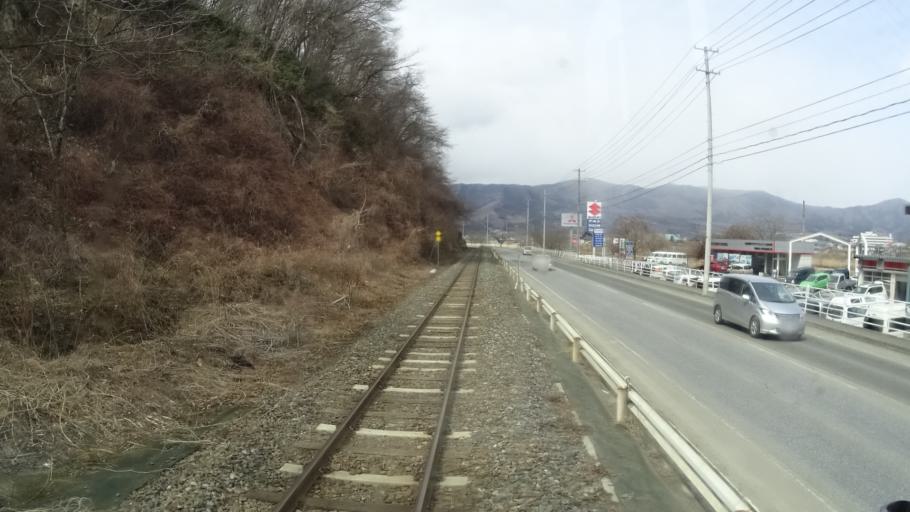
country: JP
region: Iwate
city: Tono
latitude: 39.3314
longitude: 141.5458
